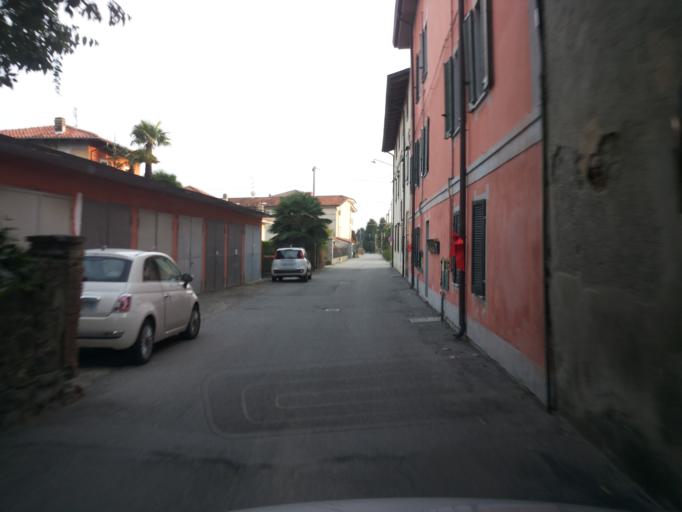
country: IT
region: Piedmont
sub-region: Provincia di Biella
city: Cavaglia
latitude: 45.4009
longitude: 8.0926
